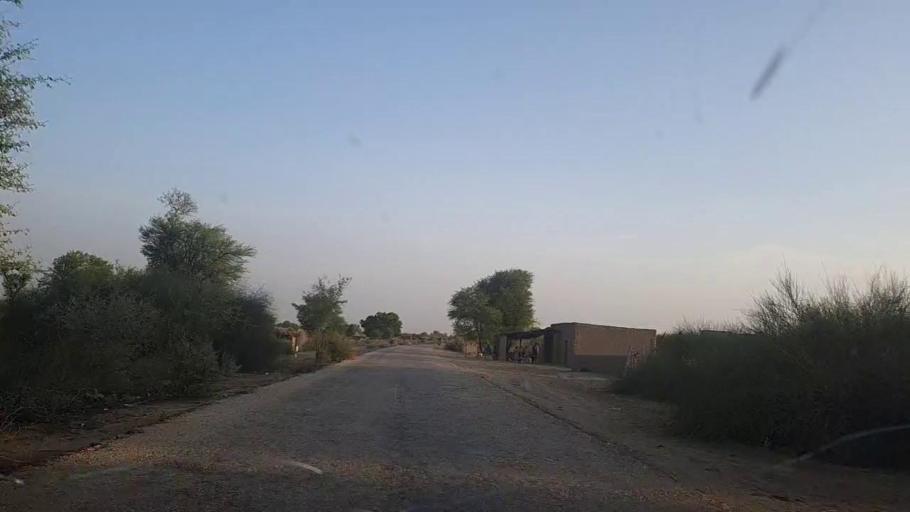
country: PK
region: Sindh
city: Khanpur
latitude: 27.6227
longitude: 69.4449
